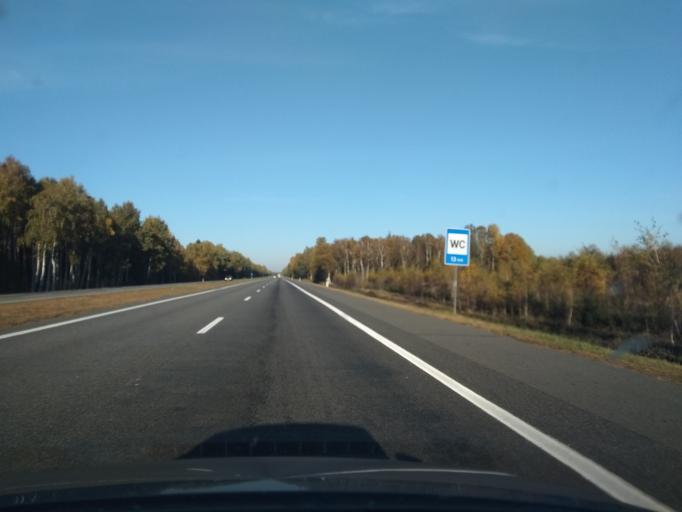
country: BY
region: Brest
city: Nyakhachava
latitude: 52.6270
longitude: 25.2053
